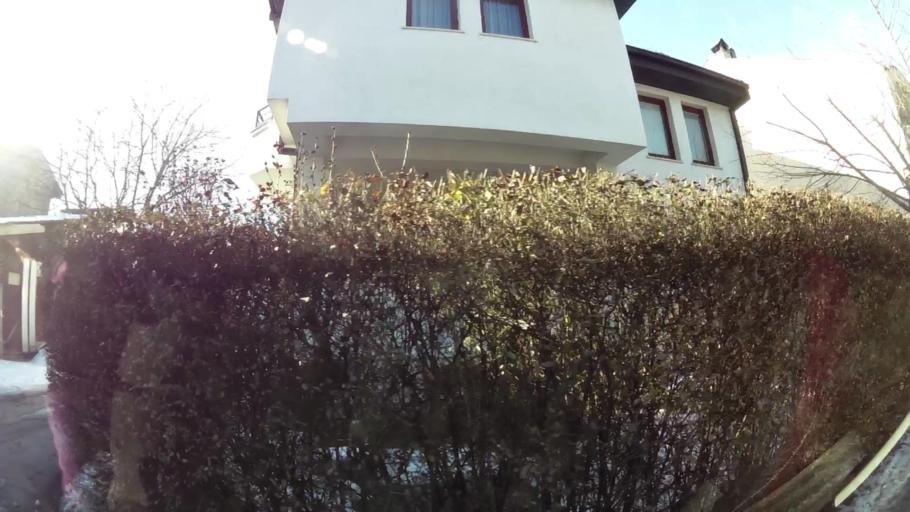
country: MK
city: Krushopek
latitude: 42.0088
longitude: 21.3747
